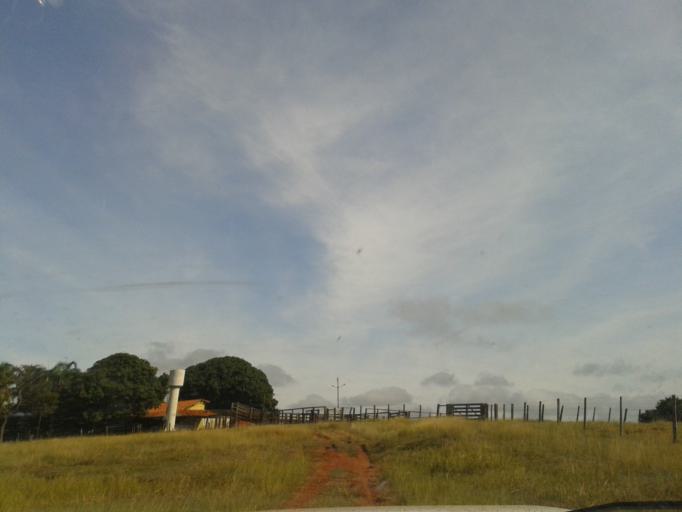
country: BR
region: Minas Gerais
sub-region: Campina Verde
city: Campina Verde
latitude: -19.4120
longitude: -49.6607
